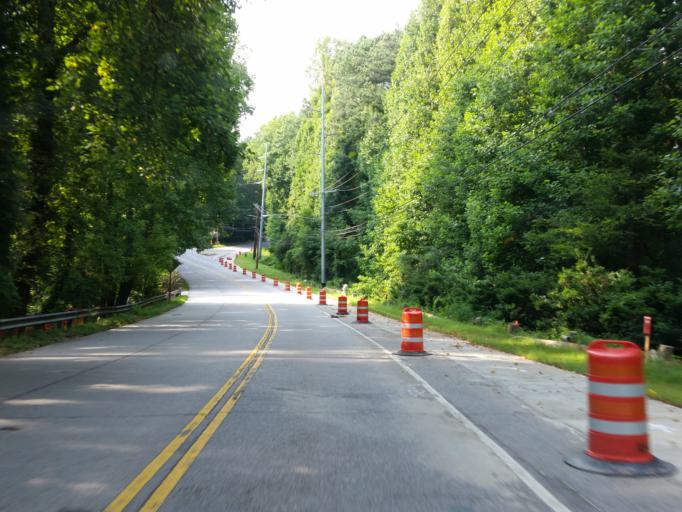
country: US
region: Georgia
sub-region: Cobb County
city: Vinings
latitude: 33.8371
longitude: -84.4074
